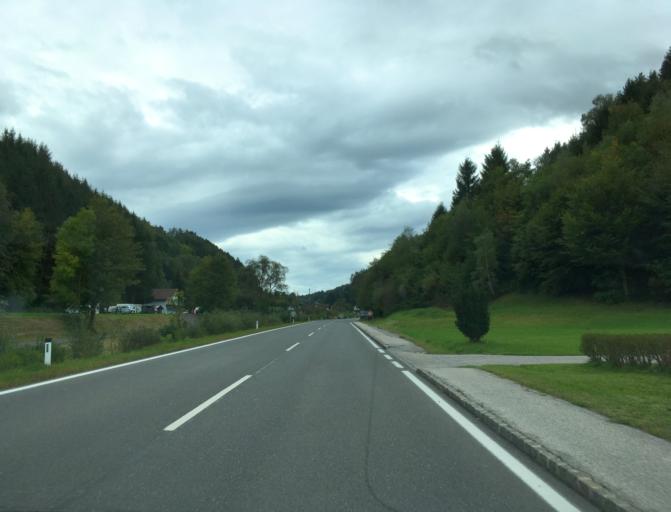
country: AT
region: Lower Austria
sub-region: Politischer Bezirk Neunkirchen
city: Thomasberg
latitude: 47.5739
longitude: 16.1430
